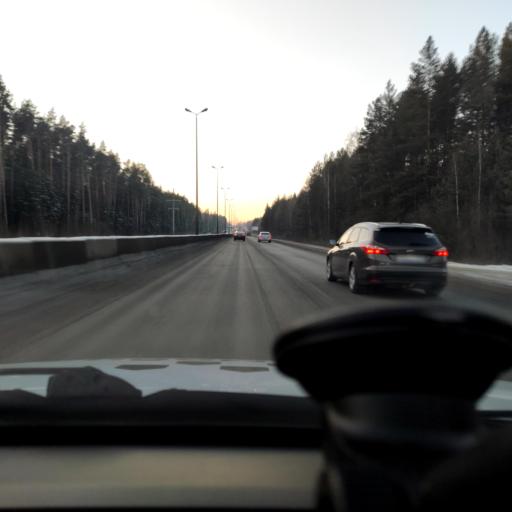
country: RU
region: Perm
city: Kondratovo
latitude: 58.0518
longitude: 56.1591
